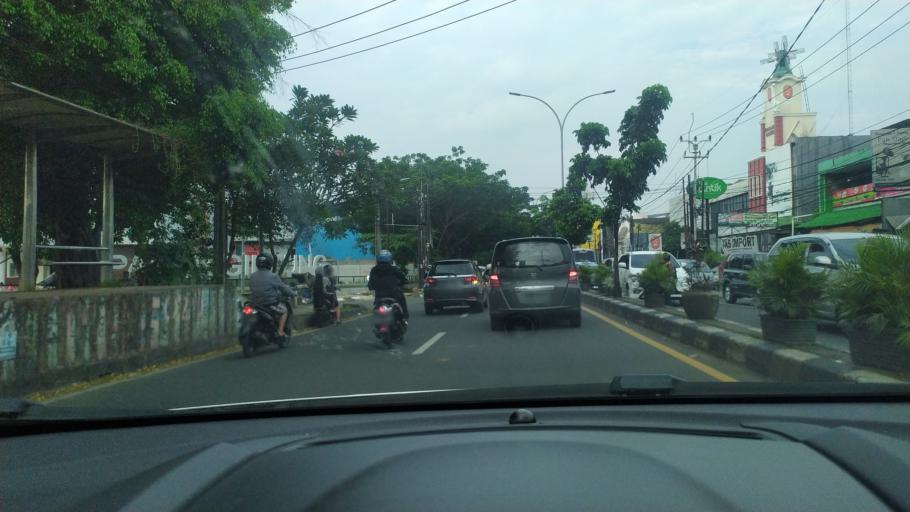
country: ID
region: Banten
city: South Tangerang
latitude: -6.3007
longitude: 106.7621
